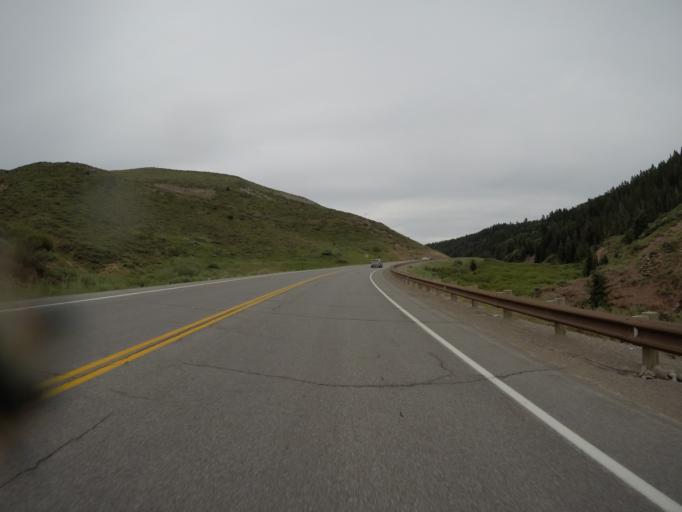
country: US
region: Wyoming
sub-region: Lincoln County
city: Afton
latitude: 42.4880
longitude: -110.9405
